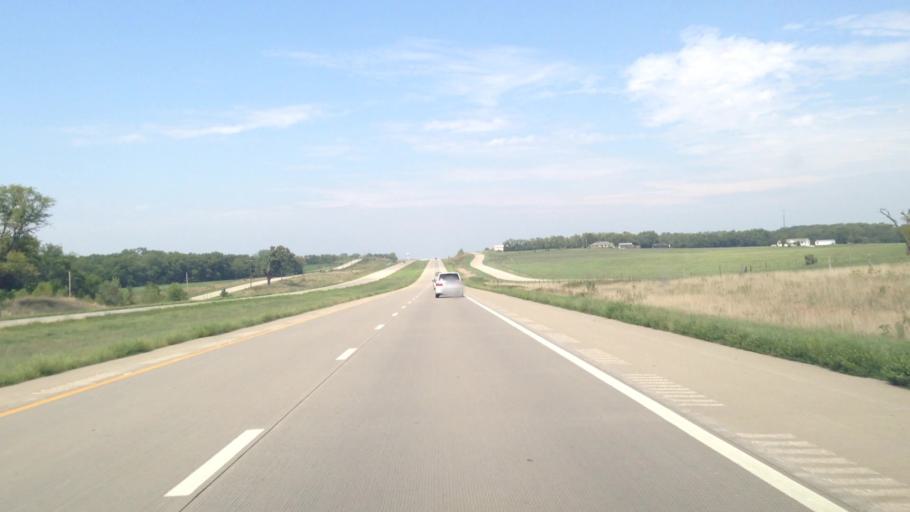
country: US
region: Kansas
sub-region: Douglas County
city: Baldwin City
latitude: 38.7954
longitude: -95.2688
